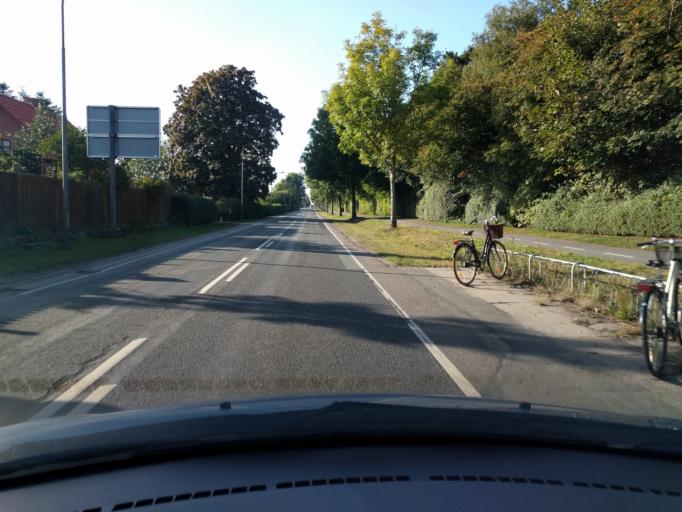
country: DK
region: South Denmark
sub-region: Odense Kommune
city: Bellinge
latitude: 55.3389
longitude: 10.3049
